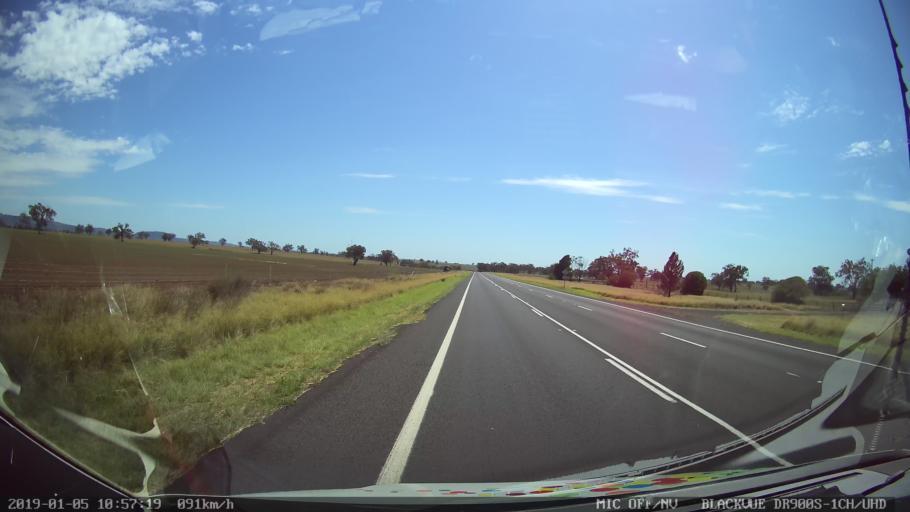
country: AU
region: New South Wales
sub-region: Warrumbungle Shire
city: Coonabarabran
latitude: -31.4324
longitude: 149.1679
